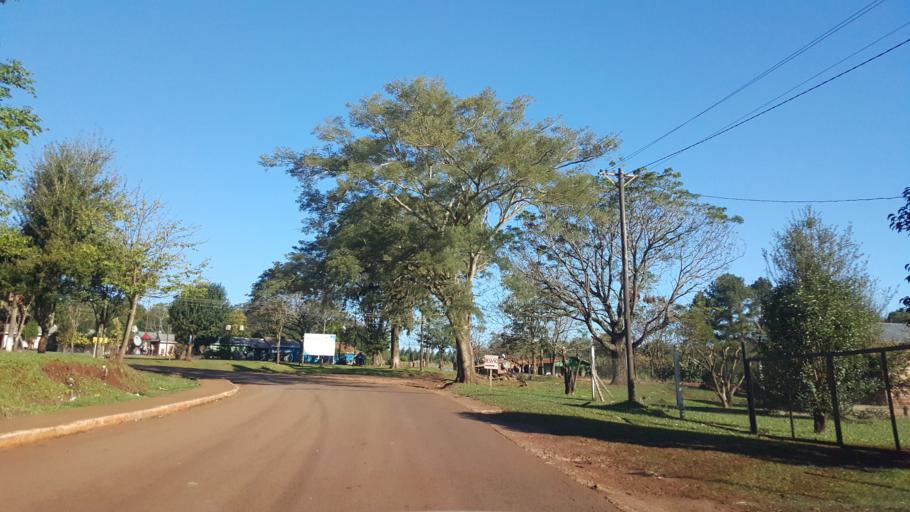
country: AR
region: Misiones
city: Jardin America
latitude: -27.0913
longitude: -55.2864
